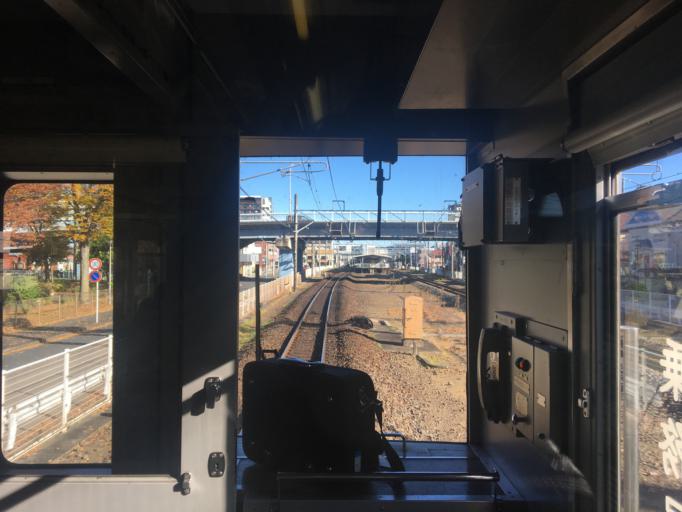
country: JP
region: Saitama
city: Sakado
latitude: 35.9699
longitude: 139.3951
